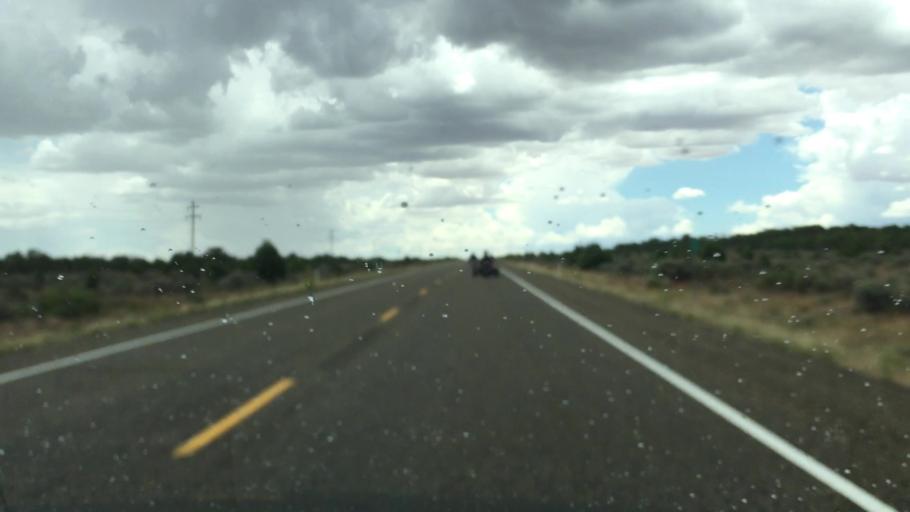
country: US
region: Utah
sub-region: Kane County
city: Kanab
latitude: 37.0836
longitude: -112.1567
